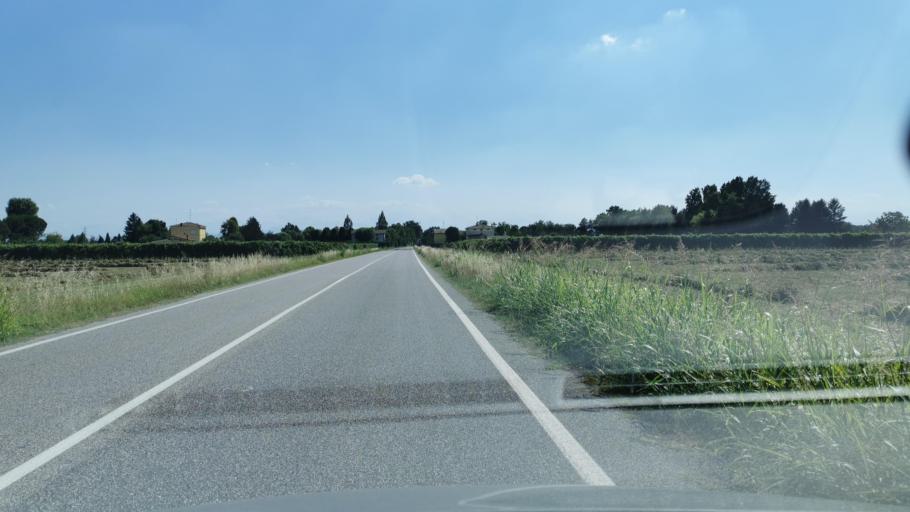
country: IT
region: Emilia-Romagna
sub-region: Provincia di Modena
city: Sam Marino
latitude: 44.7959
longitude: 10.9137
